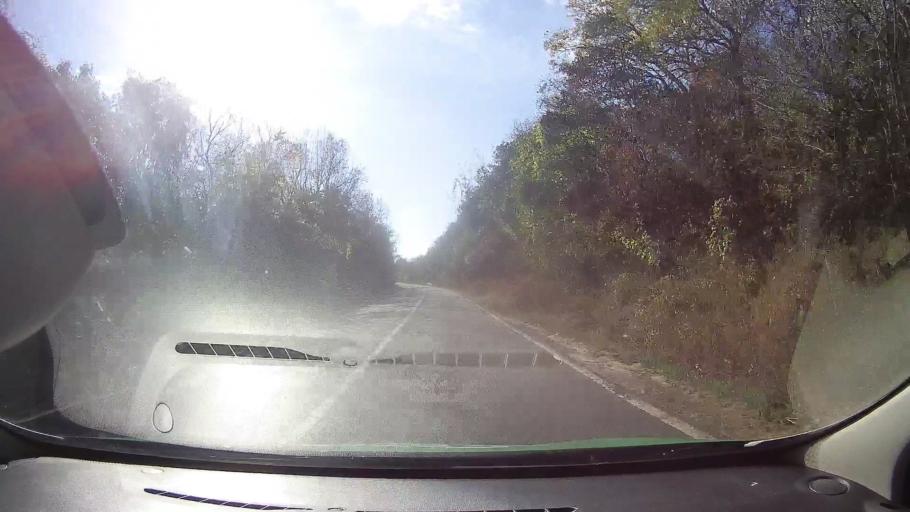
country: RO
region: Tulcea
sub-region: Oras Babadag
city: Babadag
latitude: 44.8396
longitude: 28.6963
